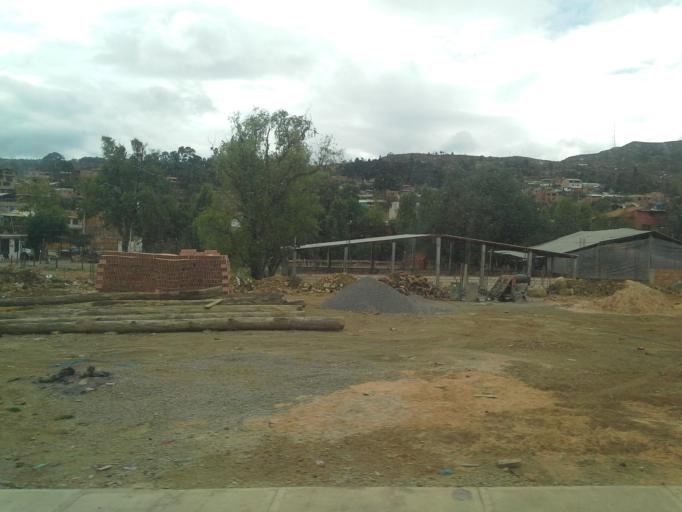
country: CO
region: Boyaca
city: Raquira
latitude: 5.5387
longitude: -73.6345
